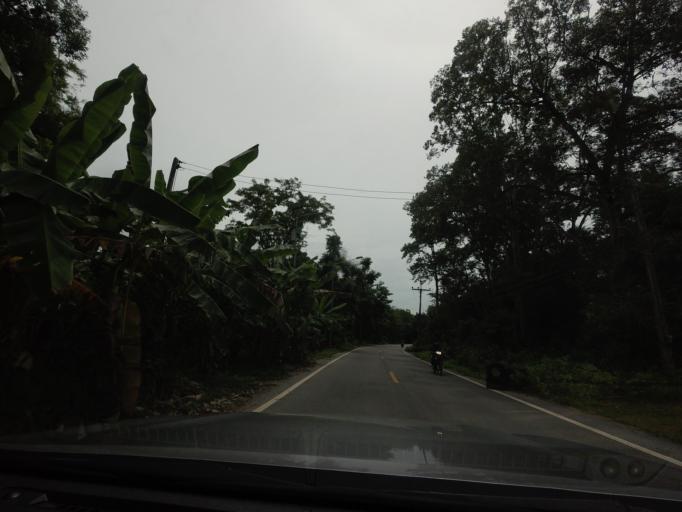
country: TH
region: Pattani
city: Kapho
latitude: 6.5990
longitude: 101.5309
